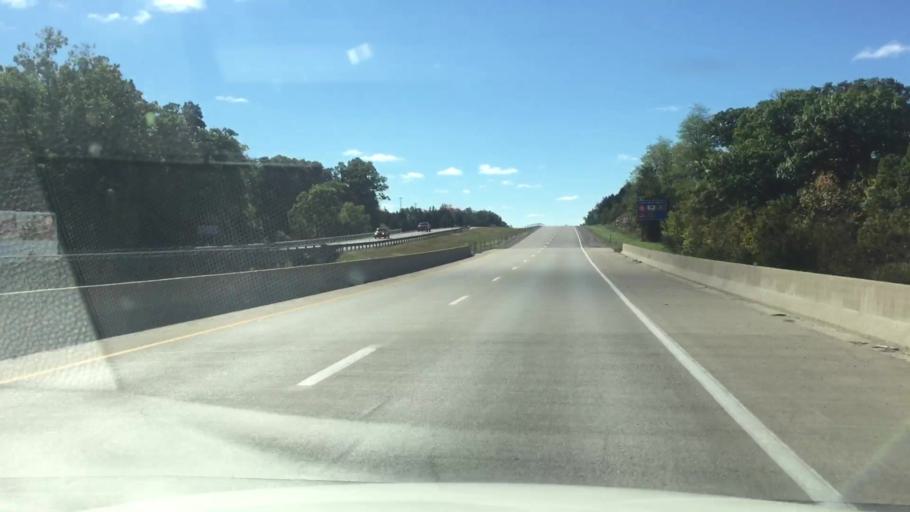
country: US
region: Missouri
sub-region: Boone County
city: Columbia
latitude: 38.9271
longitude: -92.2948
